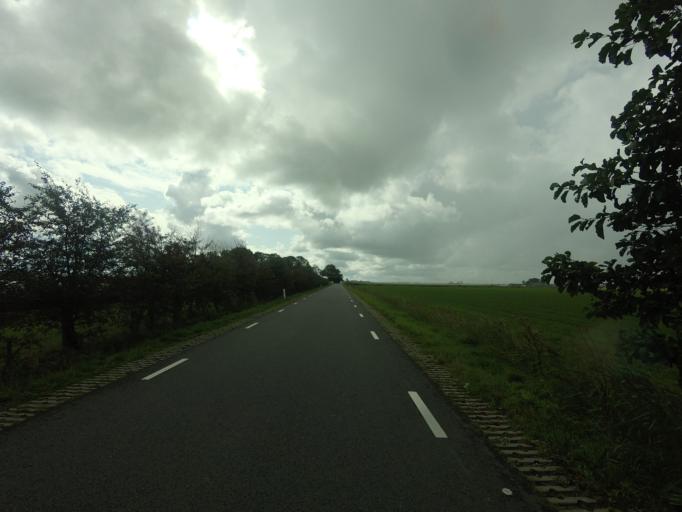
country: NL
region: Friesland
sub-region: Gemeente Boarnsterhim
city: Wergea
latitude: 53.1498
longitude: 5.8346
